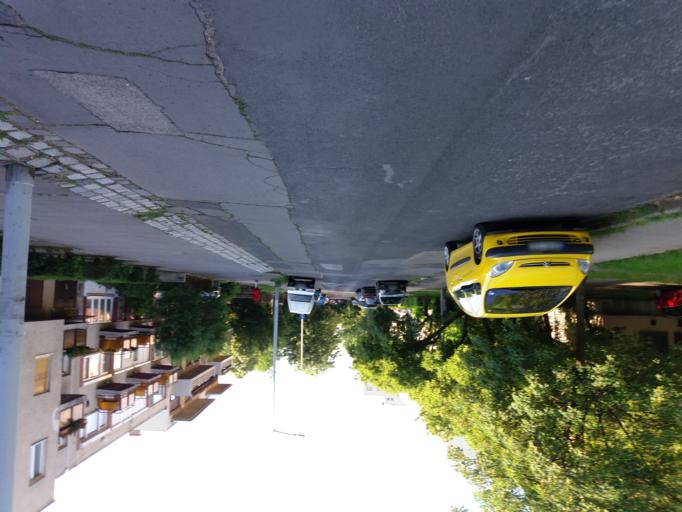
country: HU
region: Budapest
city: Budapest XI. keruelet
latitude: 47.4597
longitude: 19.0374
